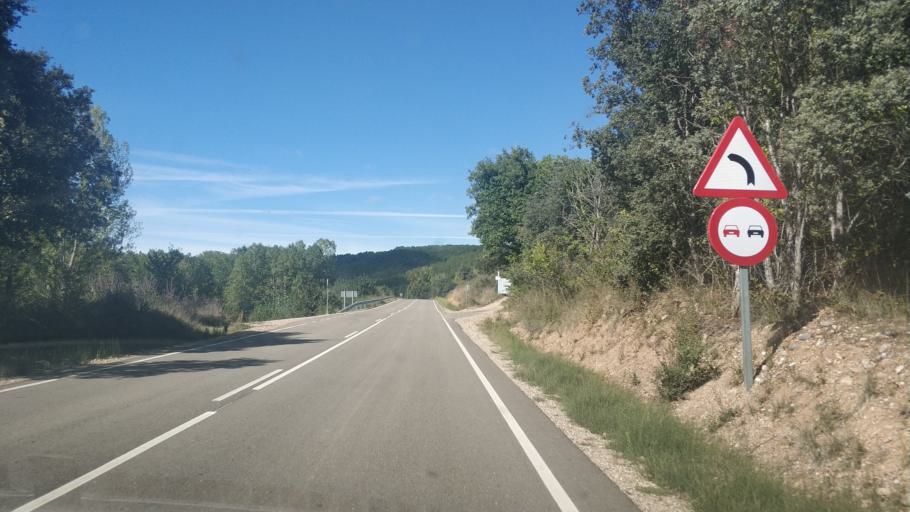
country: ES
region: Castille and Leon
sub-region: Provincia de Burgos
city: Puentedura
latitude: 42.0527
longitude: -3.5553
